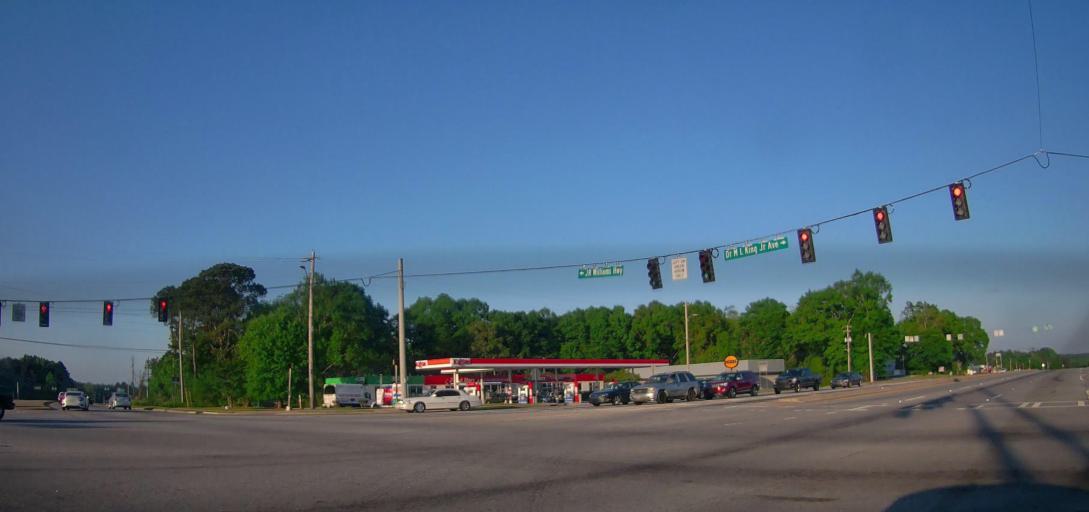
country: US
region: Georgia
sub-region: Newton County
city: Covington
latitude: 33.5993
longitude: -83.8336
